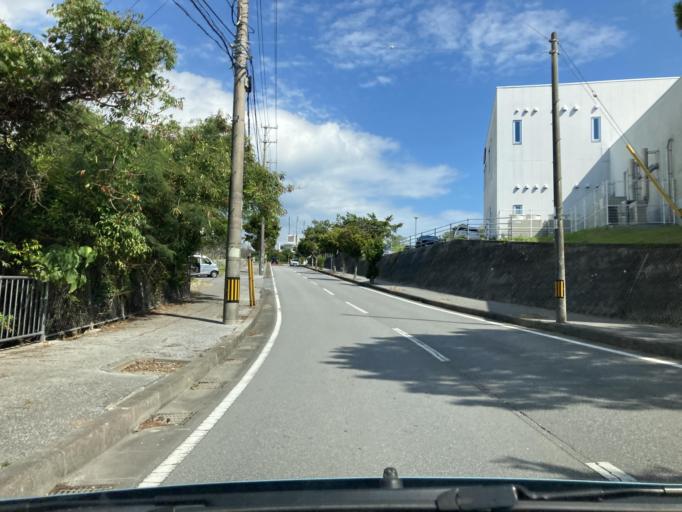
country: JP
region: Okinawa
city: Ginowan
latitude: 26.2429
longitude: 127.7589
